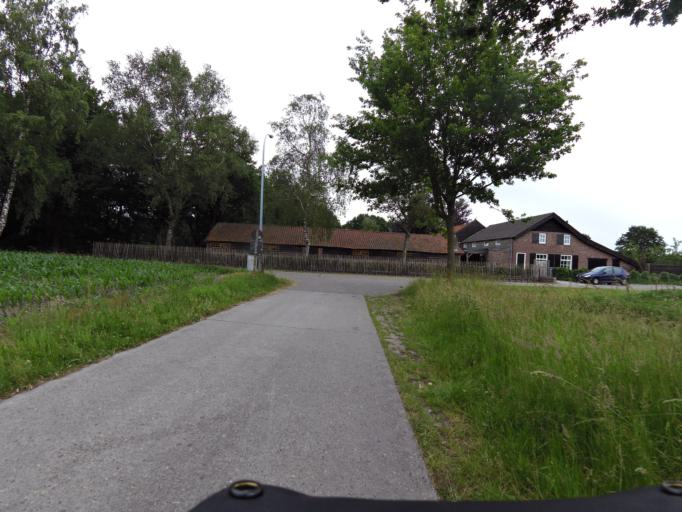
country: NL
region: North Brabant
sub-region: Gemeente Goirle
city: Goirle
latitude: 51.4645
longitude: 5.0738
